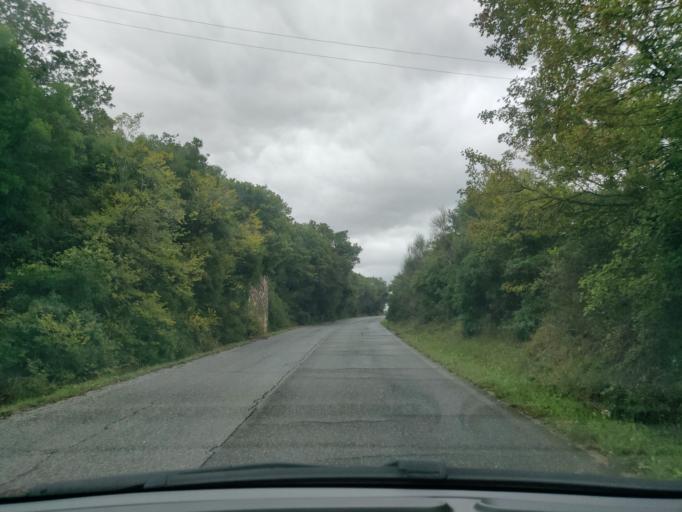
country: IT
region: Latium
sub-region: Citta metropolitana di Roma Capitale
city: Allumiere
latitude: 42.1261
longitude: 11.8582
